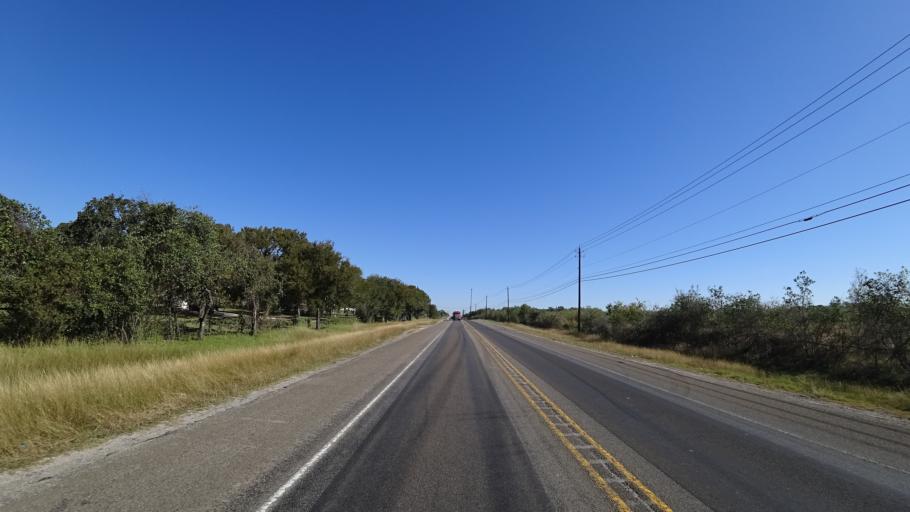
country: US
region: Texas
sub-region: Travis County
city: Hornsby Bend
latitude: 30.2700
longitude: -97.6036
